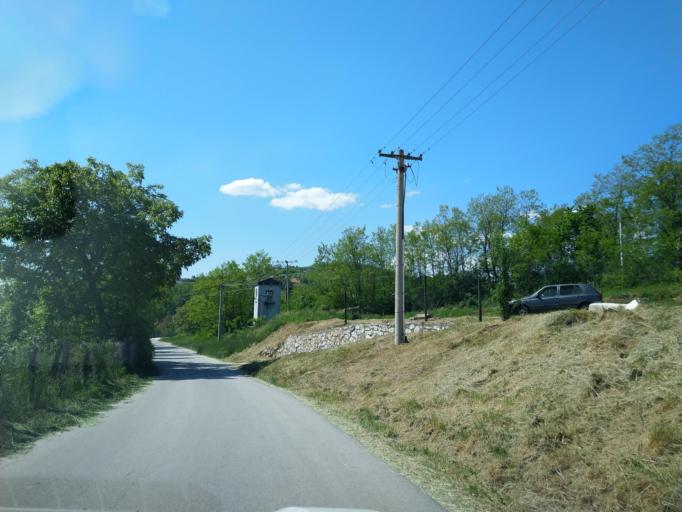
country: RS
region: Central Serbia
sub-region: Zlatiborski Okrug
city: Uzice
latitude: 43.8604
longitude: 19.9066
